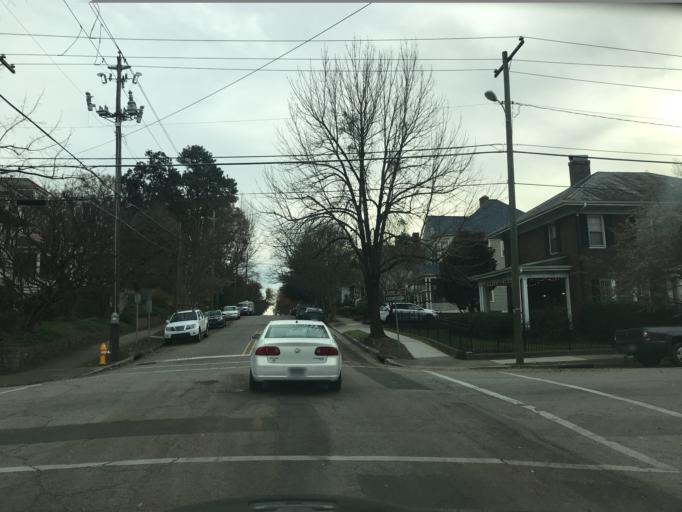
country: US
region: North Carolina
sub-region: Wake County
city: Raleigh
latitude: 35.7838
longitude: -78.6321
